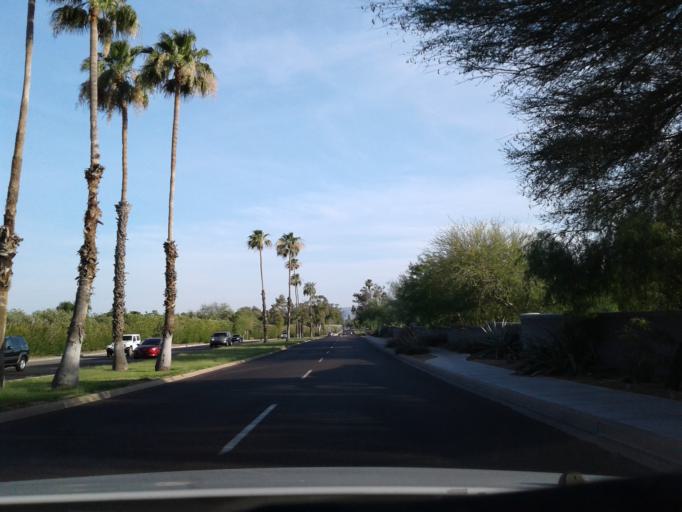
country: US
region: Arizona
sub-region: Maricopa County
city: Phoenix
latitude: 33.5232
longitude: -112.0301
